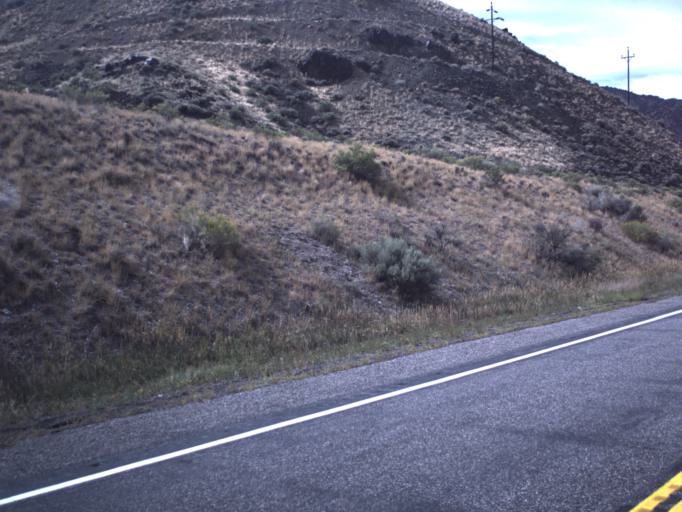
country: US
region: Utah
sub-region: Sevier County
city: Monroe
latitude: 38.4937
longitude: -112.2492
